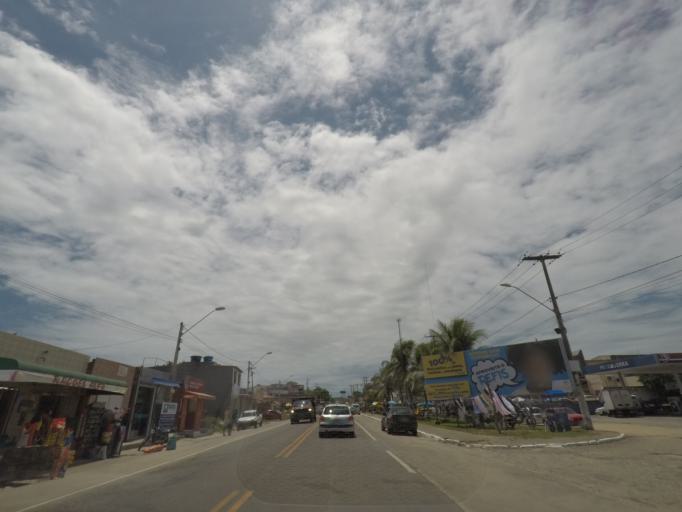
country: BR
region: Bahia
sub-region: Itaparica
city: Itaparica
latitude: -12.9322
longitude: -38.6229
